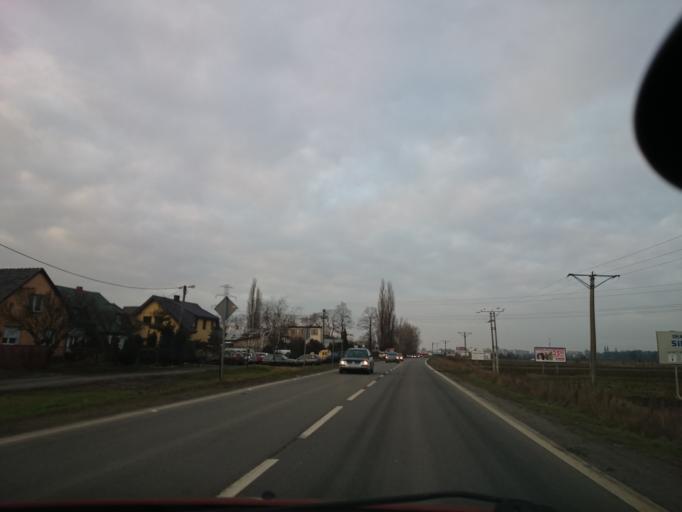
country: PL
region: Opole Voivodeship
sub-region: Powiat opolski
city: Opole
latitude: 50.6456
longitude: 17.9109
